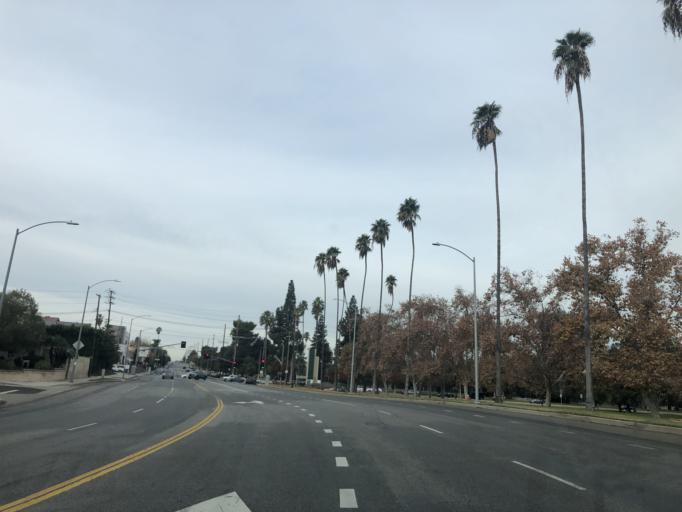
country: US
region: California
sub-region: Los Angeles County
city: Van Nuys
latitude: 34.1722
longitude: -118.4995
